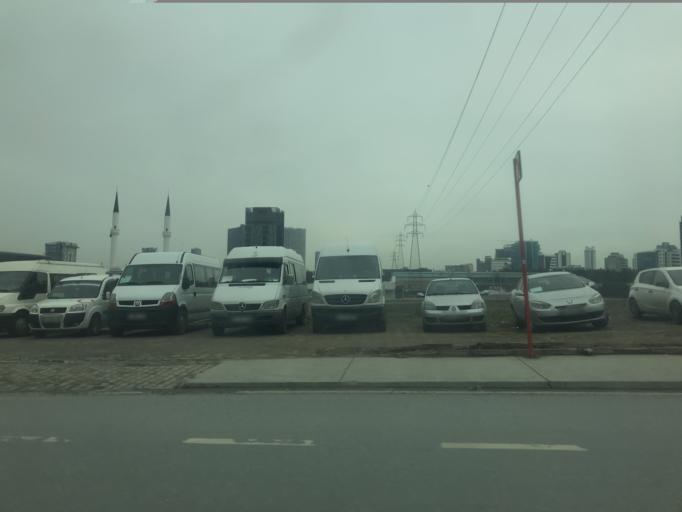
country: TR
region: Istanbul
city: Mahmutbey
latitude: 41.0454
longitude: 28.8137
